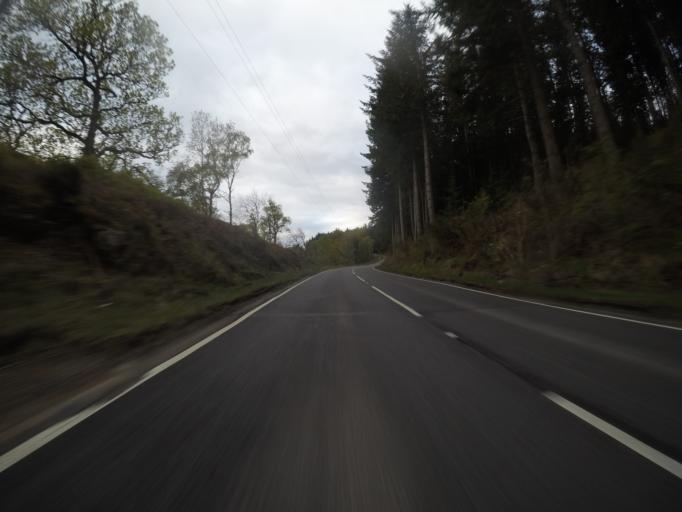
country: GB
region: Scotland
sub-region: Highland
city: Beauly
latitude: 57.1652
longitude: -4.6520
